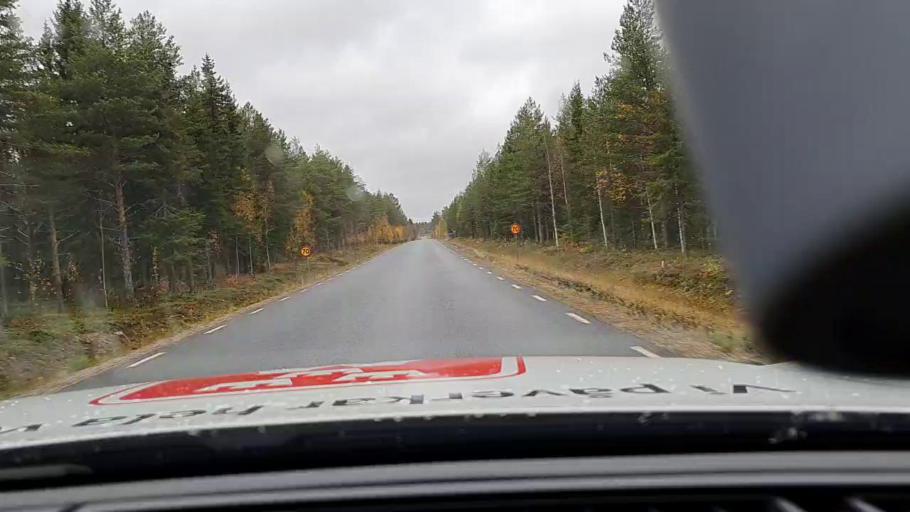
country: SE
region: Norrbotten
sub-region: Haparanda Kommun
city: Haparanda
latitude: 65.9411
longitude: 23.8019
